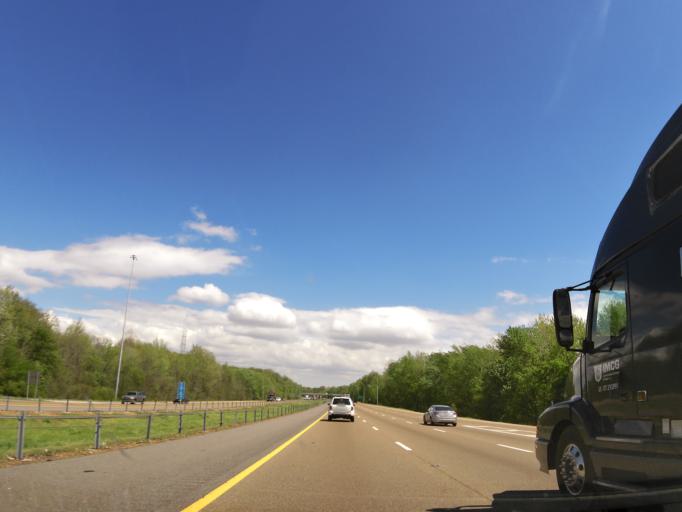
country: US
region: Tennessee
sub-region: Shelby County
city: Bartlett
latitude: 35.1902
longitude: -89.9530
